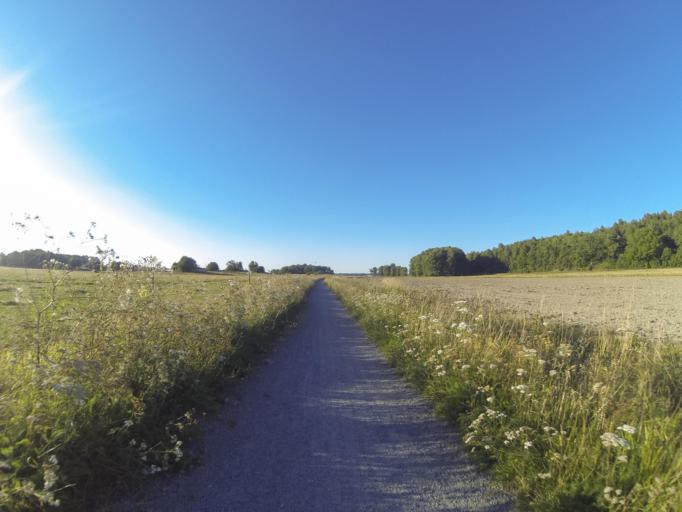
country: SE
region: Vaestmanland
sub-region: Vasteras
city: Vasteras
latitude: 59.5674
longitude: 16.6494
